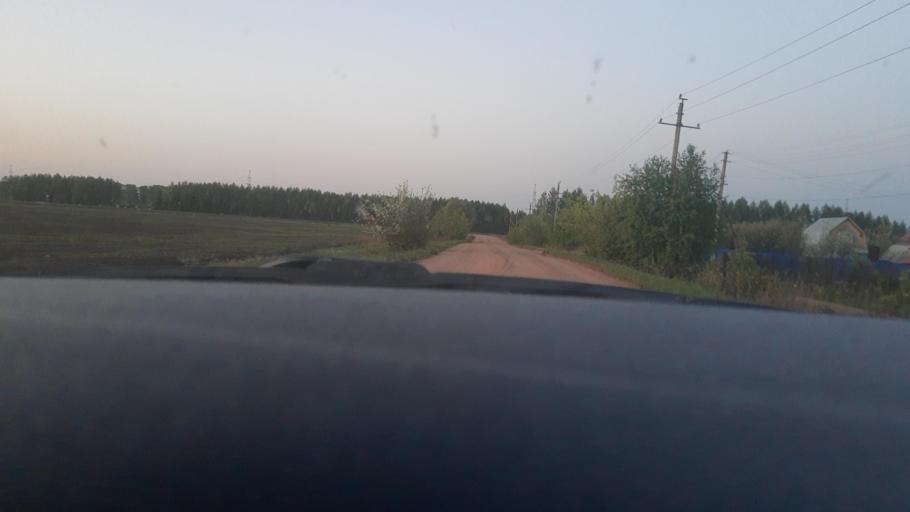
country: RU
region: Bashkortostan
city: Iglino
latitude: 54.7542
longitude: 56.3361
